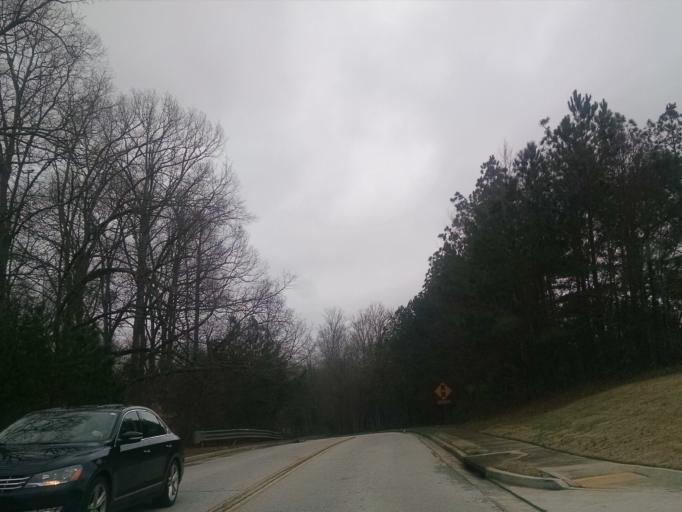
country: US
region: Georgia
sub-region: Gwinnett County
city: Sugar Hill
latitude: 34.1005
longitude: -84.0385
